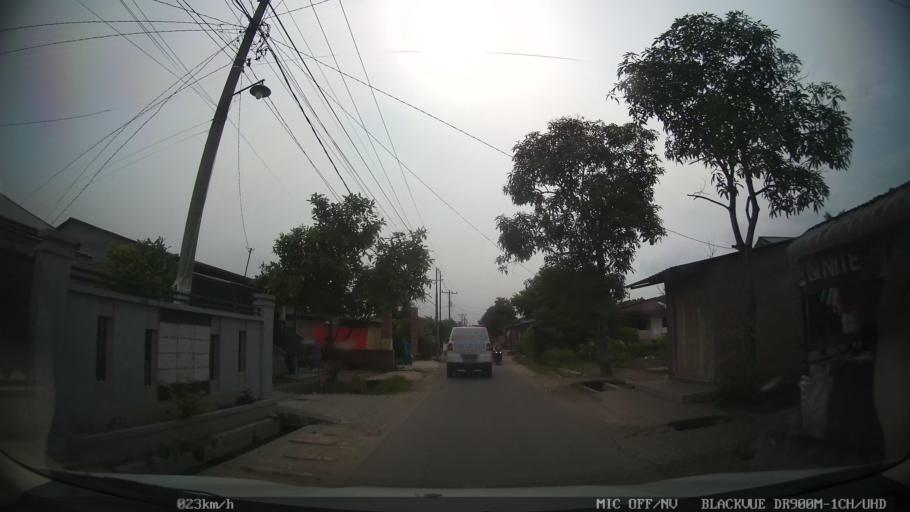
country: ID
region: North Sumatra
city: Medan
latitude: 3.5694
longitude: 98.7551
